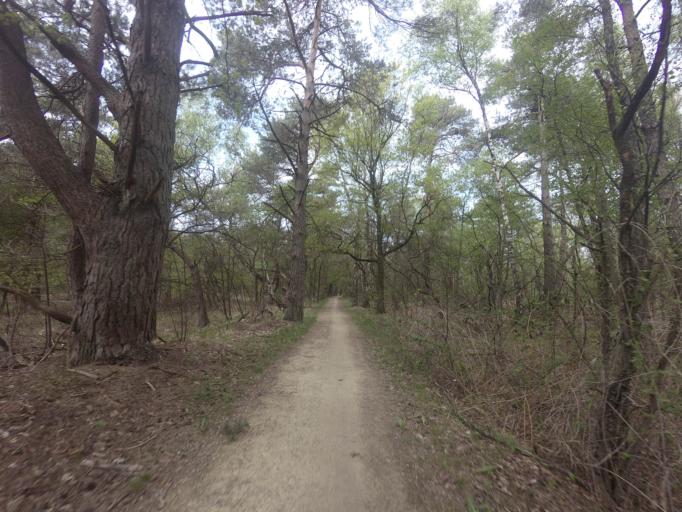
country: NL
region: Overijssel
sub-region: Gemeente Hof van Twente
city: Delden
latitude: 52.2214
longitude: 6.7316
